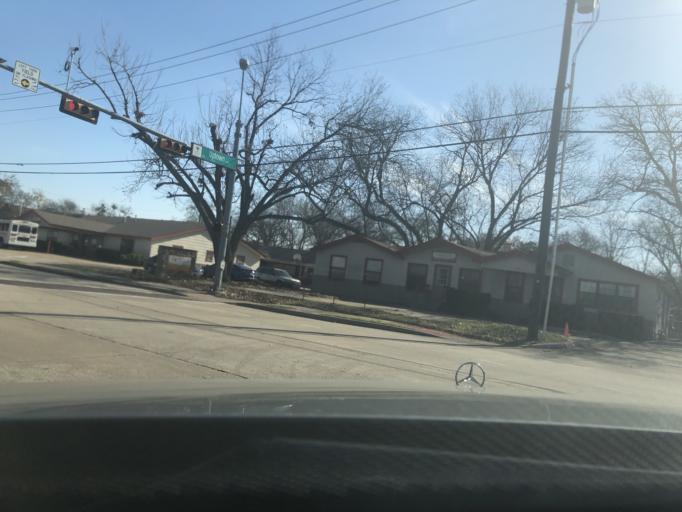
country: US
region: Texas
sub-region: Dallas County
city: Cedar Hill
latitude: 32.5901
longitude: -96.9522
